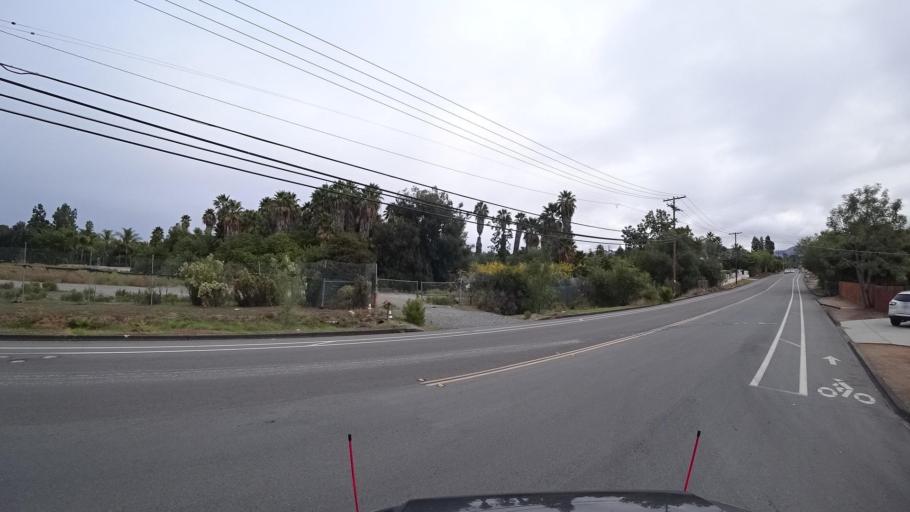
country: US
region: California
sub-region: San Diego County
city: Rancho San Diego
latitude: 32.7621
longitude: -116.9261
